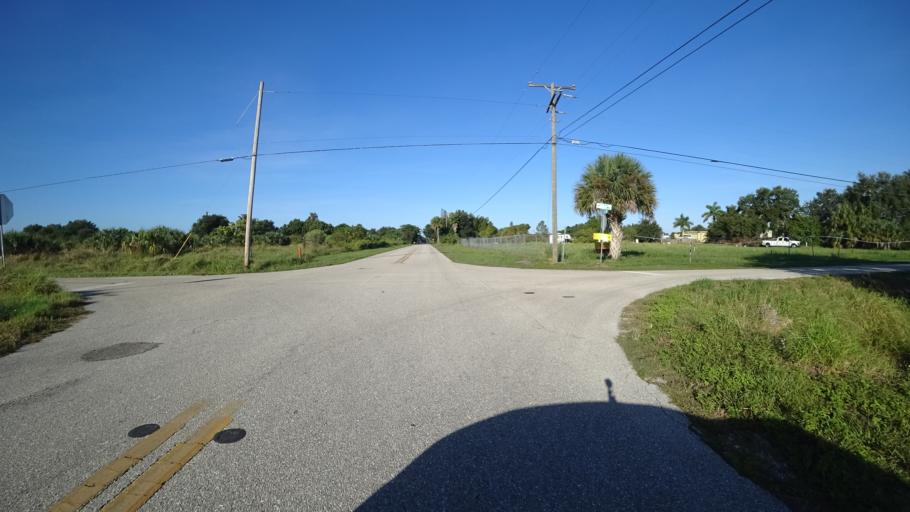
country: US
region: Florida
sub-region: Manatee County
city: Memphis
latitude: 27.5682
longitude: -82.5481
